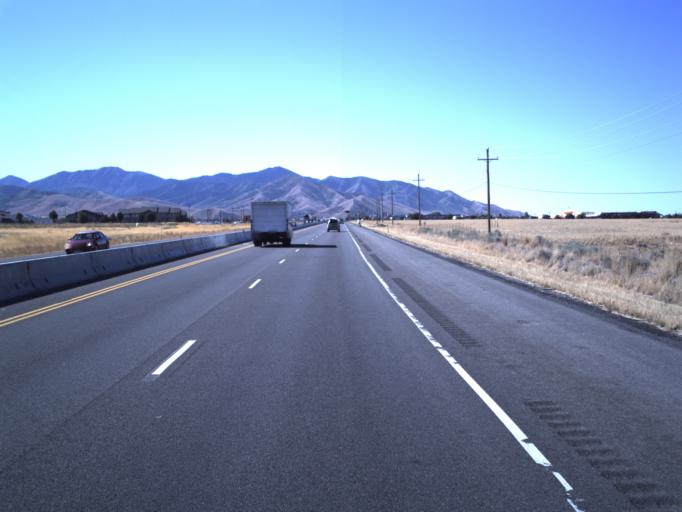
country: US
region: Utah
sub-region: Tooele County
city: Erda
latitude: 40.5796
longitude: -112.2941
